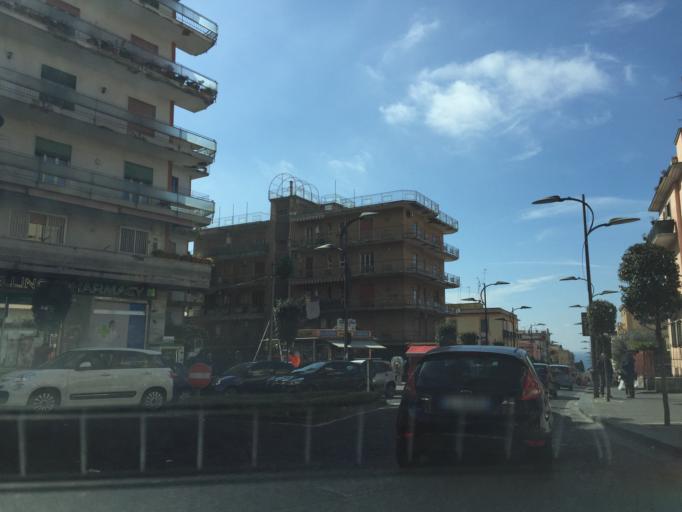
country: IT
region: Campania
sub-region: Provincia di Napoli
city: Ercolano
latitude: 40.8086
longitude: 14.3537
